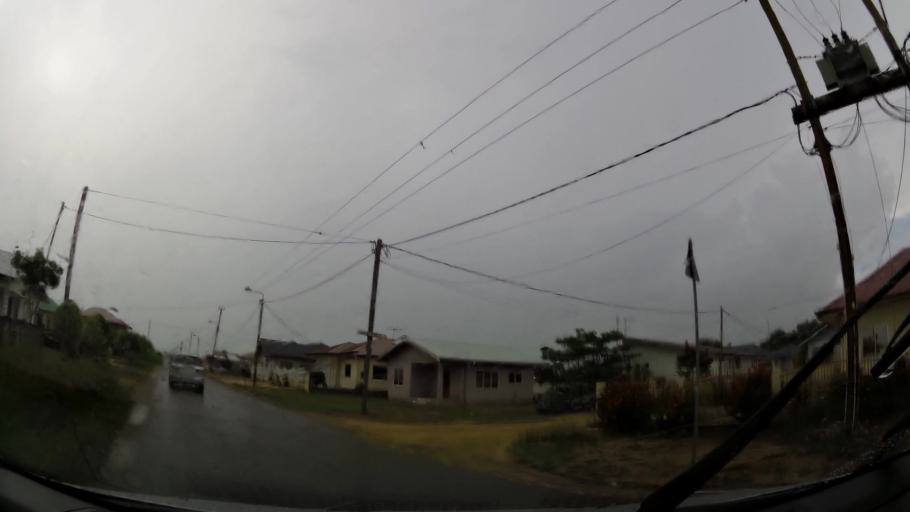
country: SR
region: Commewijne
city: Nieuw Amsterdam
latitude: 5.8537
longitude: -55.1180
